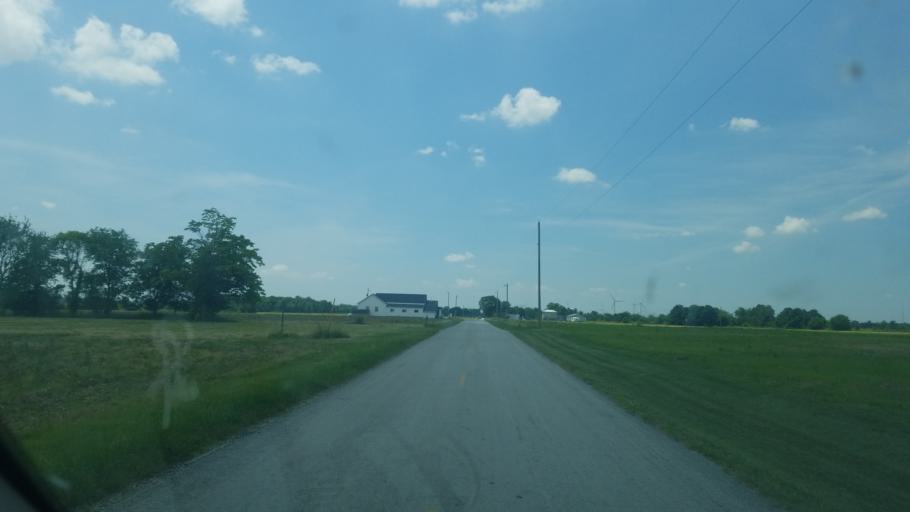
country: US
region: Ohio
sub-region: Hardin County
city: Forest
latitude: 40.7897
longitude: -83.6114
